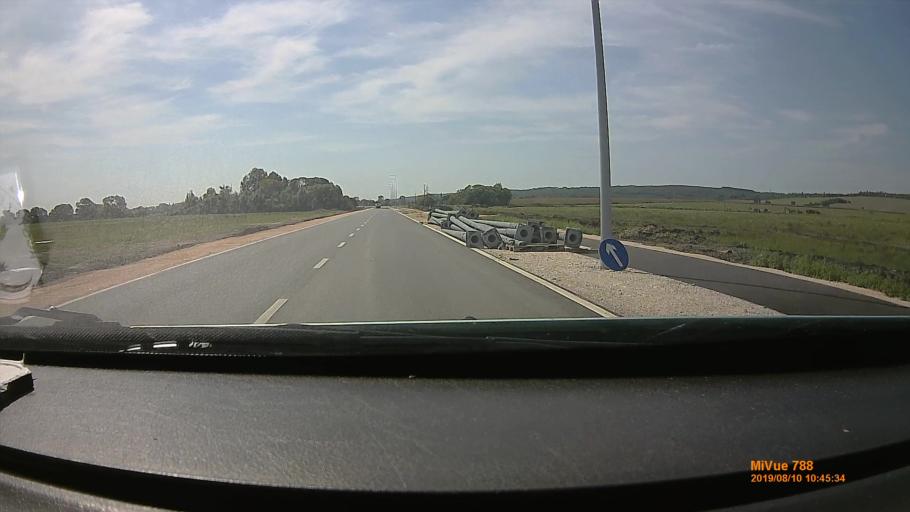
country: HU
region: Borsod-Abauj-Zemplen
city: Malyi
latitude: 48.0530
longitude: 20.8098
